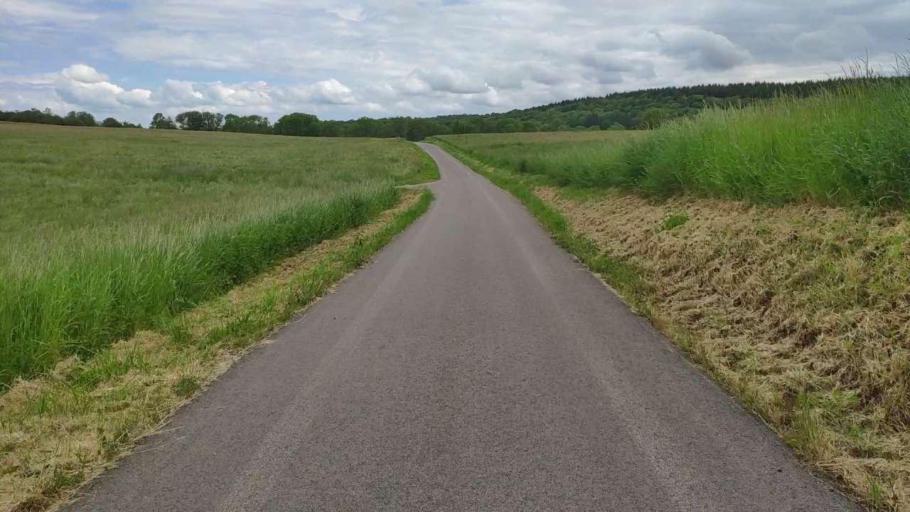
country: FR
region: Franche-Comte
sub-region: Departement du Jura
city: Poligny
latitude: 46.7626
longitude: 5.6498
